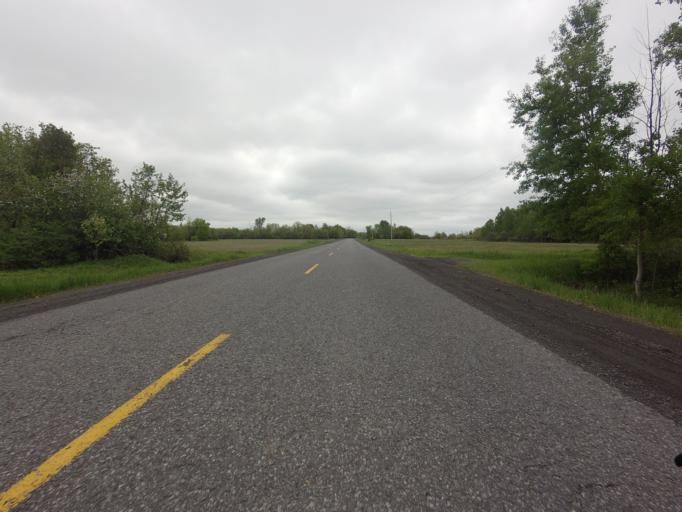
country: US
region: New York
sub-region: St. Lawrence County
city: Norfolk
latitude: 44.9856
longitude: -75.1577
